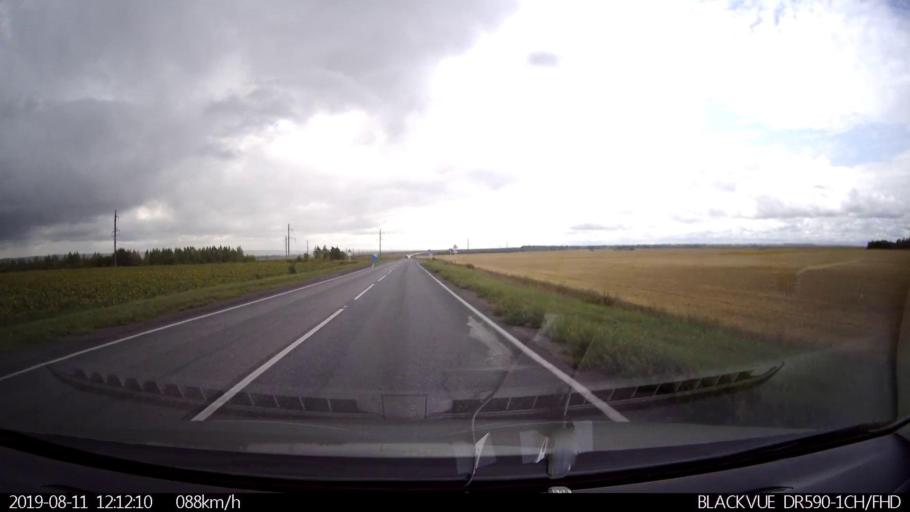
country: RU
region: Ulyanovsk
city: Silikatnyy
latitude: 53.9766
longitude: 47.9978
